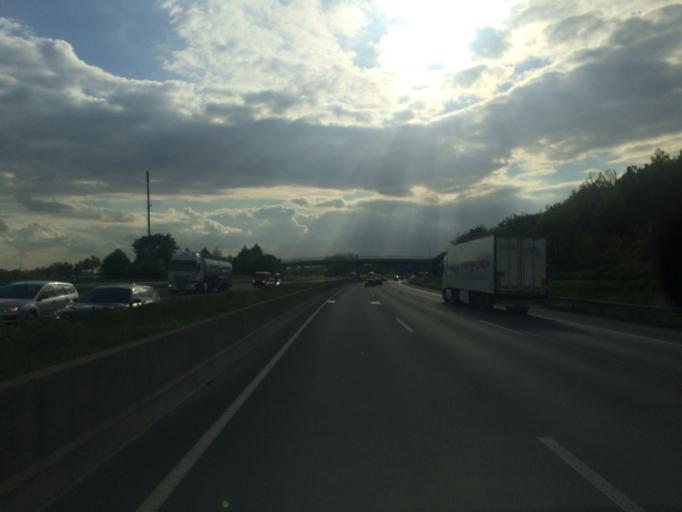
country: DE
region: North Rhine-Westphalia
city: Kamen
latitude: 51.6015
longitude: 7.7122
